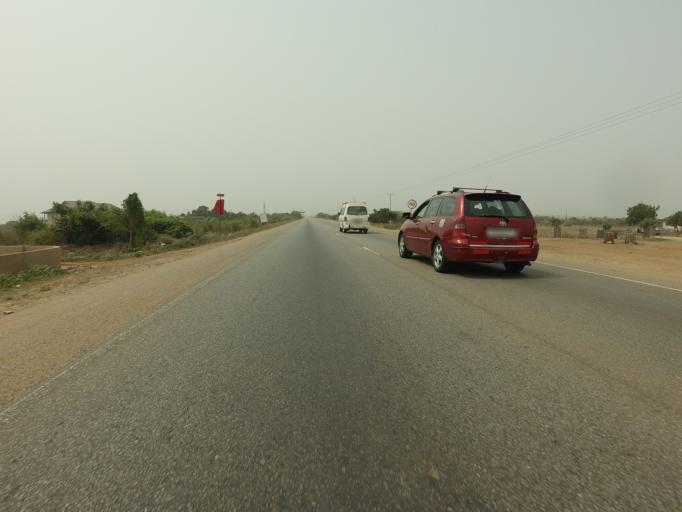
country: GH
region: Greater Accra
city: Tema
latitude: 5.8330
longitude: 0.2133
